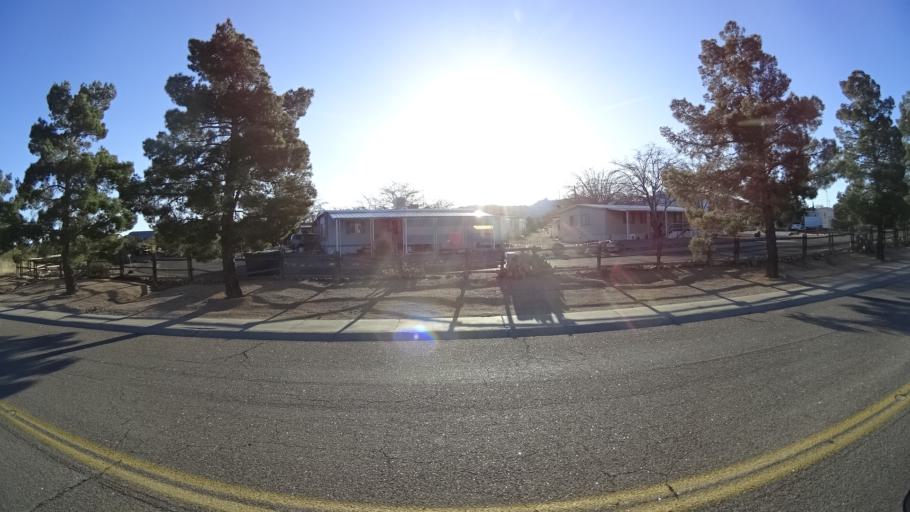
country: US
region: Arizona
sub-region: Mohave County
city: Kingman
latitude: 35.1911
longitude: -114.0115
